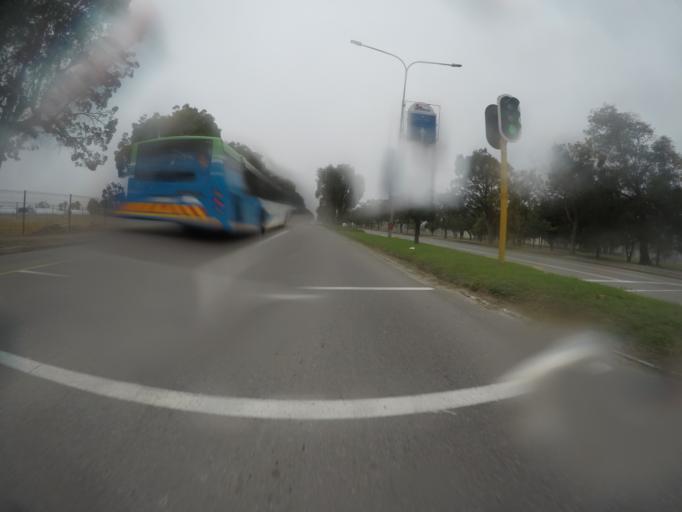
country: ZA
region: Western Cape
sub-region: Eden District Municipality
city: George
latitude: -33.9756
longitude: 22.4435
